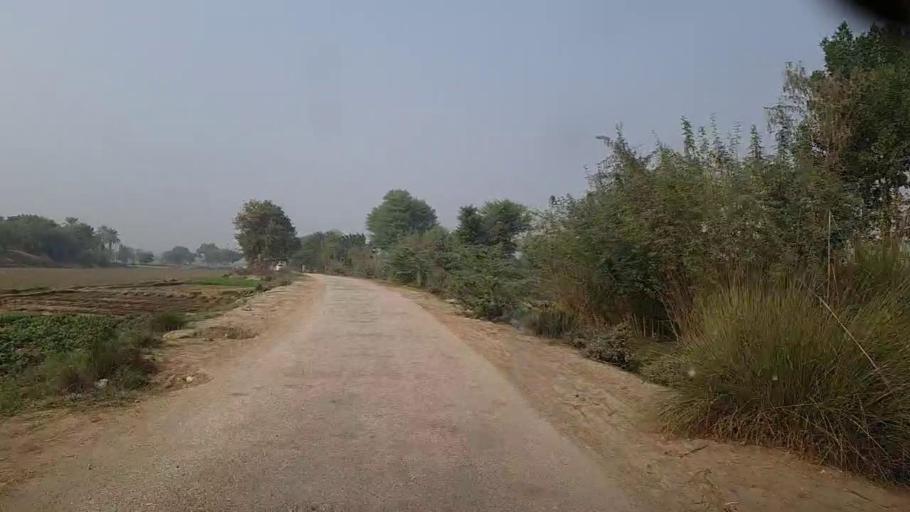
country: PK
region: Sindh
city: Bozdar
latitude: 27.0685
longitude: 68.6368
